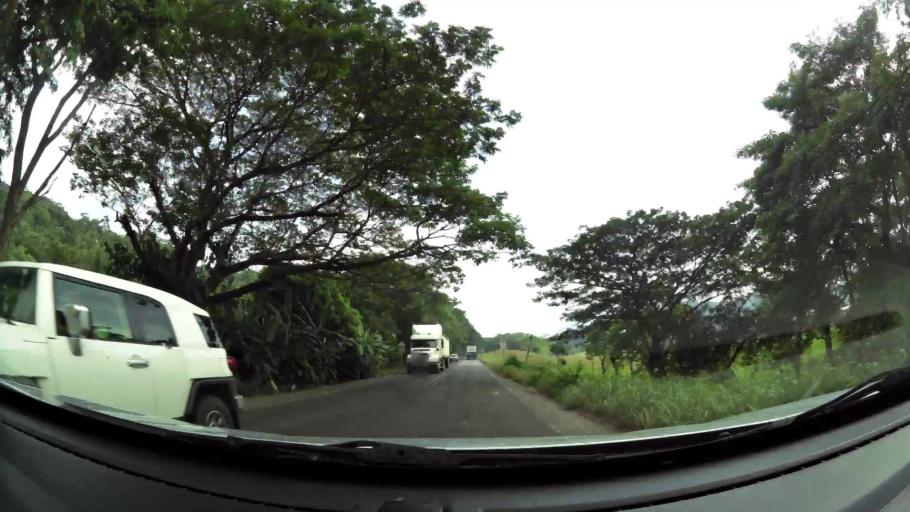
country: CR
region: Guanacaste
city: Juntas
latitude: 10.1956
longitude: -84.9530
